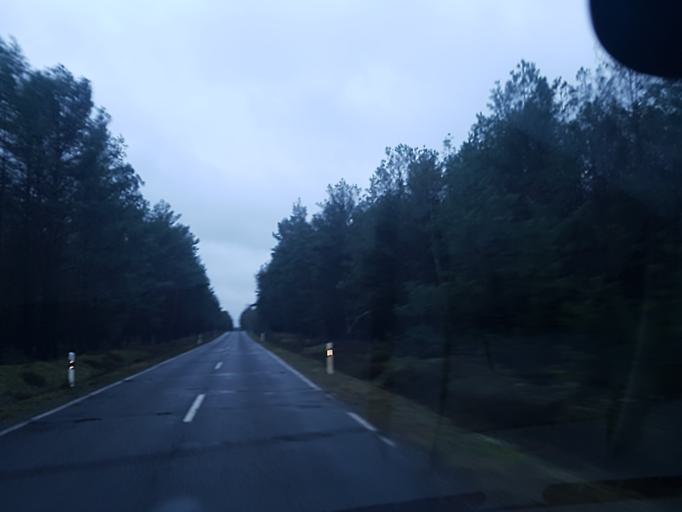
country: DE
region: Brandenburg
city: Schonewalde
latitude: 51.6206
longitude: 13.6379
